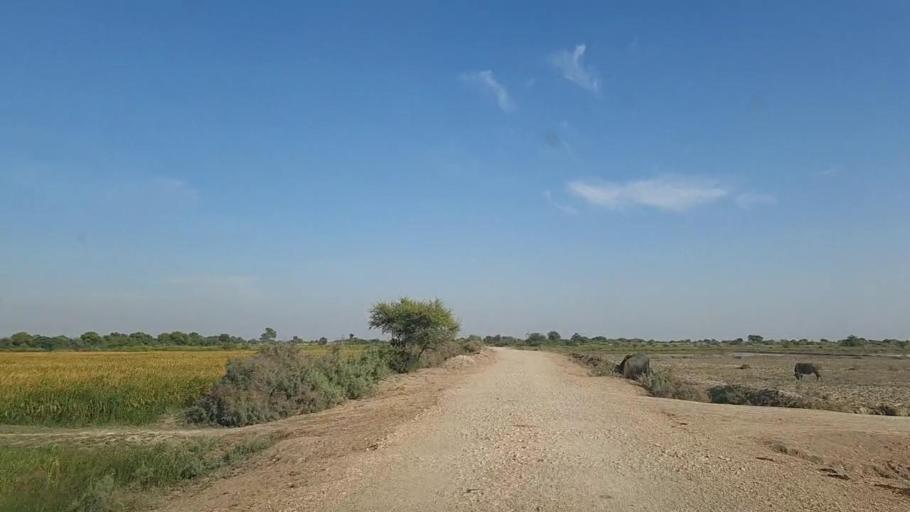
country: PK
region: Sindh
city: Mirpur Batoro
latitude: 24.7614
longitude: 68.3596
